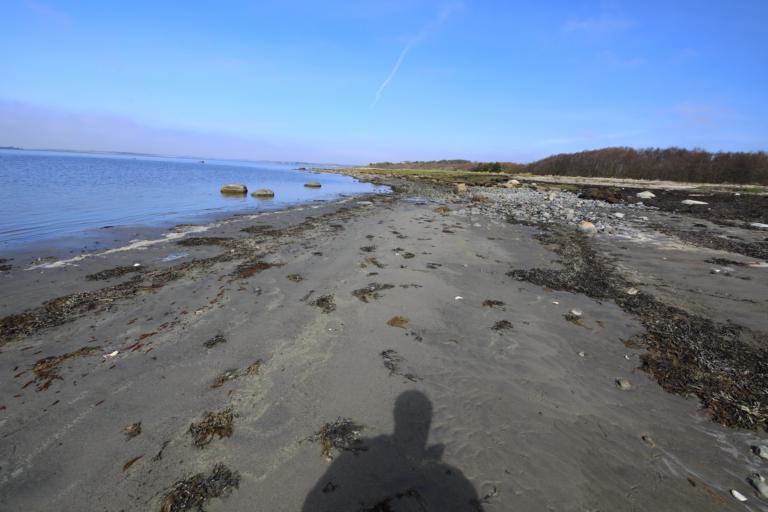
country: SE
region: Halland
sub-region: Kungsbacka Kommun
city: Frillesas
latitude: 57.2850
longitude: 12.1638
